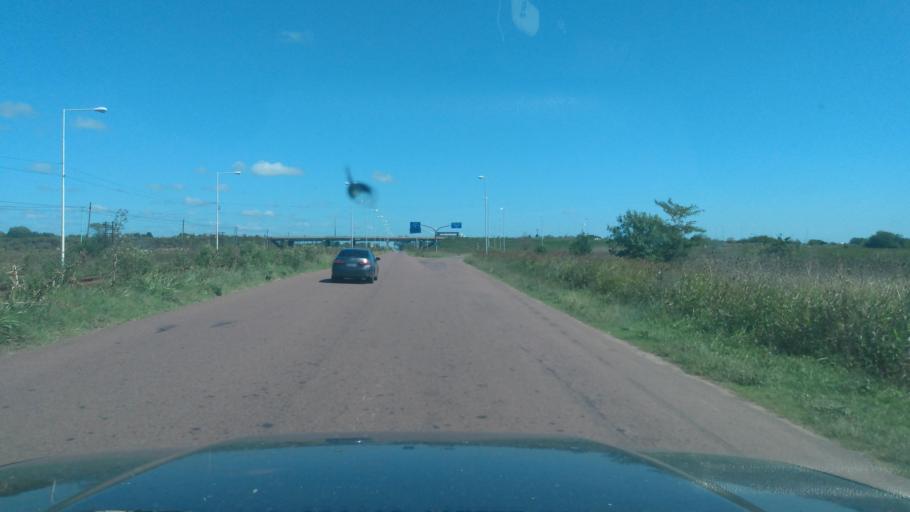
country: AR
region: Buenos Aires
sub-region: Partido de Lujan
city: Lujan
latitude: -34.5897
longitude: -59.0332
